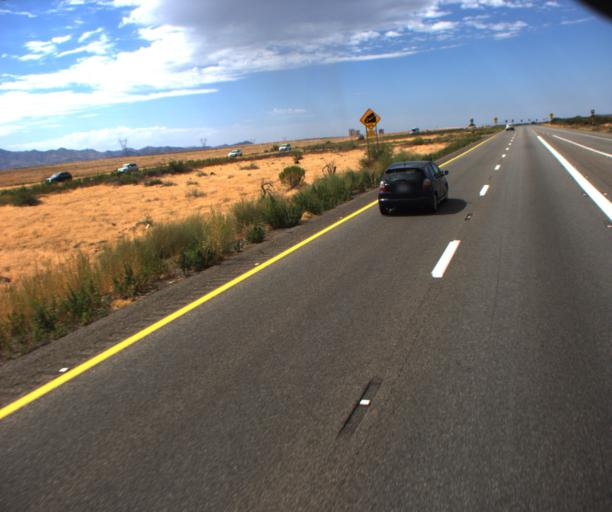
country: US
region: Arizona
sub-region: Yavapai County
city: Black Canyon City
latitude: 34.1799
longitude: -112.1350
